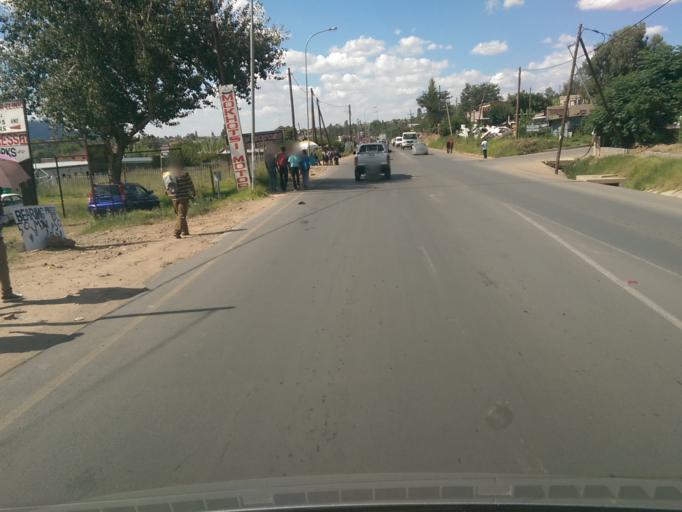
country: LS
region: Maseru
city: Maseru
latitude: -29.3085
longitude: 27.5137
